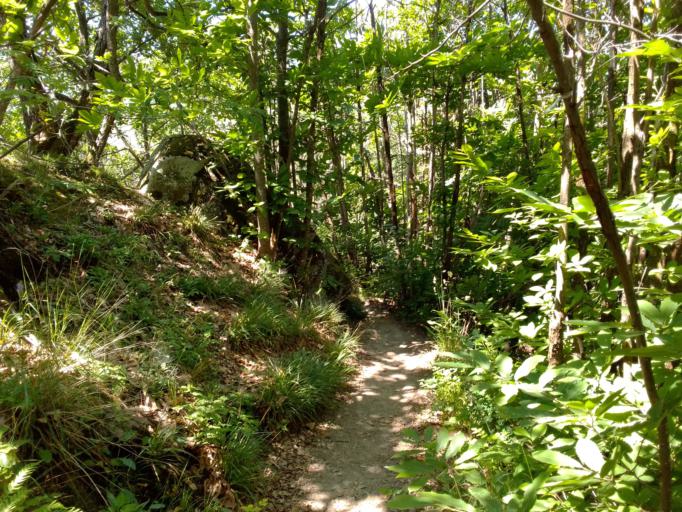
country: IT
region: Emilia-Romagna
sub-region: Provincia di Piacenza
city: Pecorara
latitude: 44.9073
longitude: 9.4013
